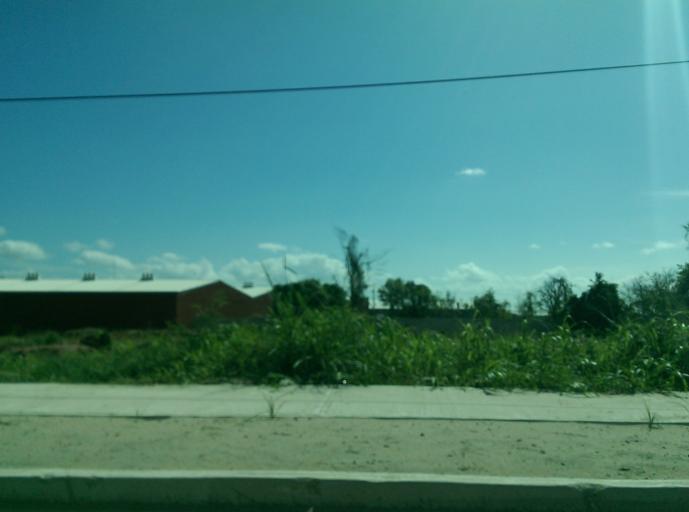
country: MX
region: Tabasco
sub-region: Centro
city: Anacleto Canabal 2da. Seccion
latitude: 17.9857
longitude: -92.9935
